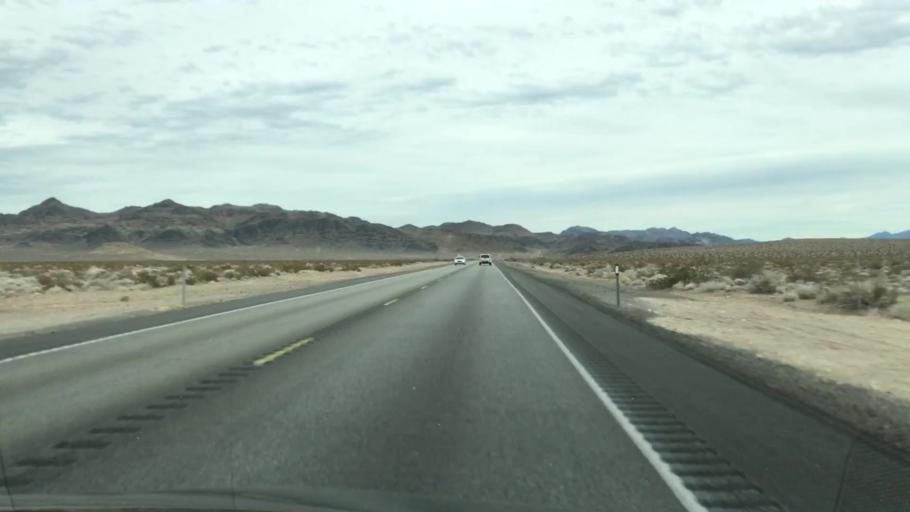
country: US
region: Nevada
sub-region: Nye County
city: Beatty
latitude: 36.6316
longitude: -116.3290
